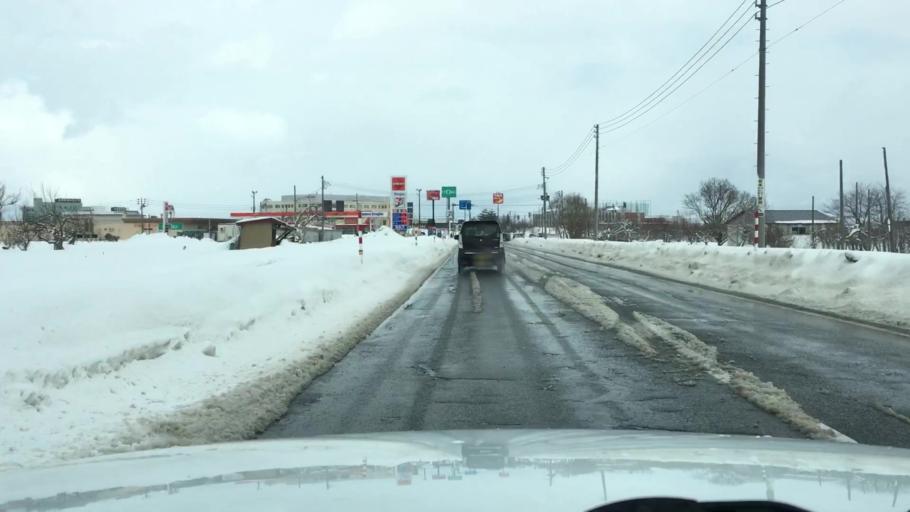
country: JP
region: Aomori
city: Hirosaki
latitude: 40.5827
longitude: 140.4982
